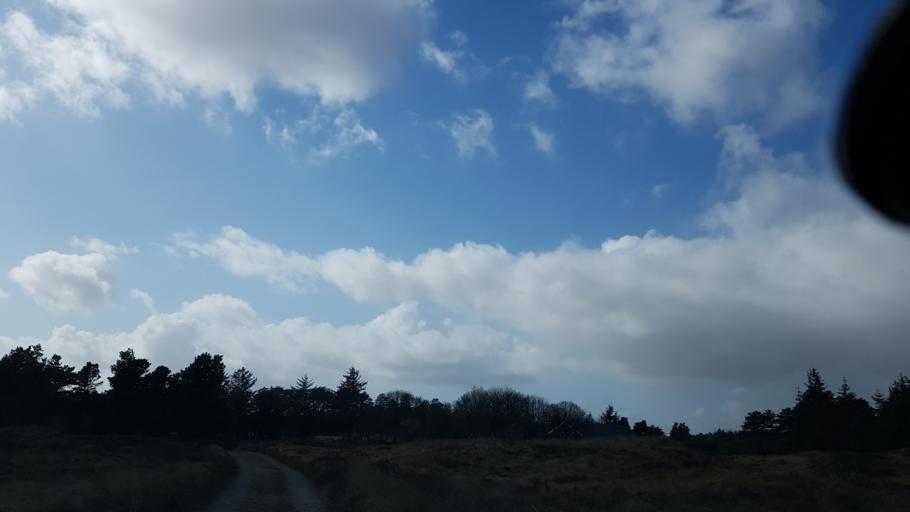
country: DE
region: Schleswig-Holstein
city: List
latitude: 55.1010
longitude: 8.5357
